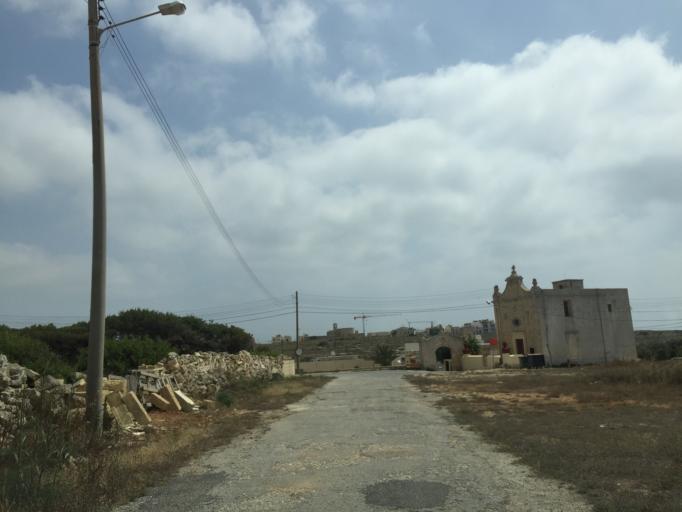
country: MT
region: L-Imgarr
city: Imgarr
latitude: 35.9004
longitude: 14.3499
